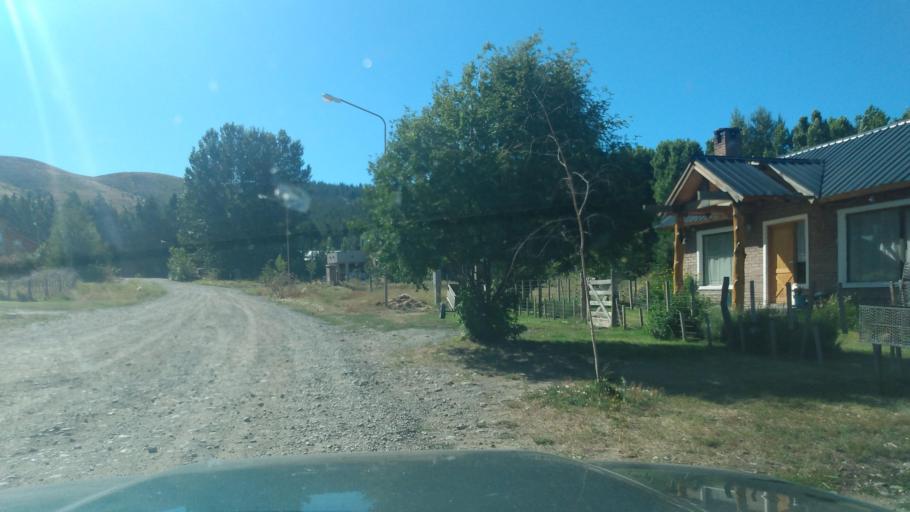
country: AR
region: Neuquen
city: Junin de los Andes
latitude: -39.9630
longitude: -71.0838
